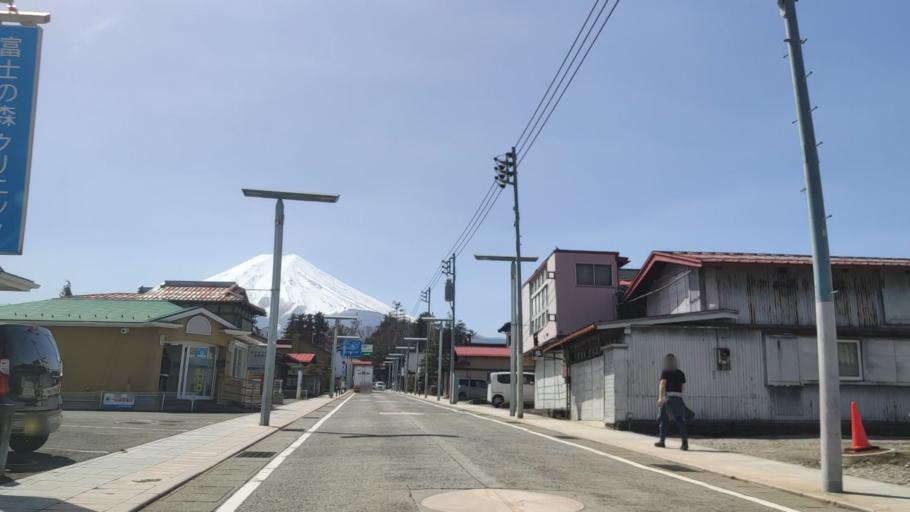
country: JP
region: Yamanashi
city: Fujikawaguchiko
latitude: 35.4763
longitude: 138.7928
